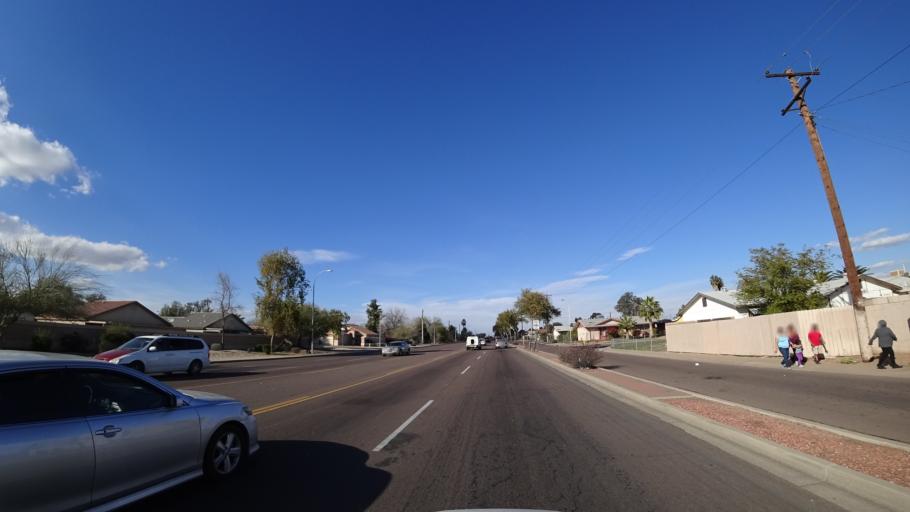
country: US
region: Arizona
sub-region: Maricopa County
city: Tolleson
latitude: 33.4816
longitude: -112.2377
